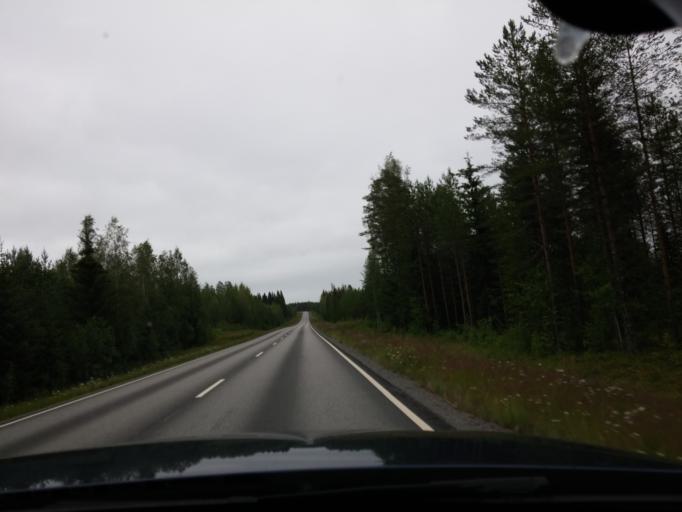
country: FI
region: Central Finland
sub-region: Saarijaervi-Viitasaari
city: Saarijaervi
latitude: 62.6791
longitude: 25.2018
